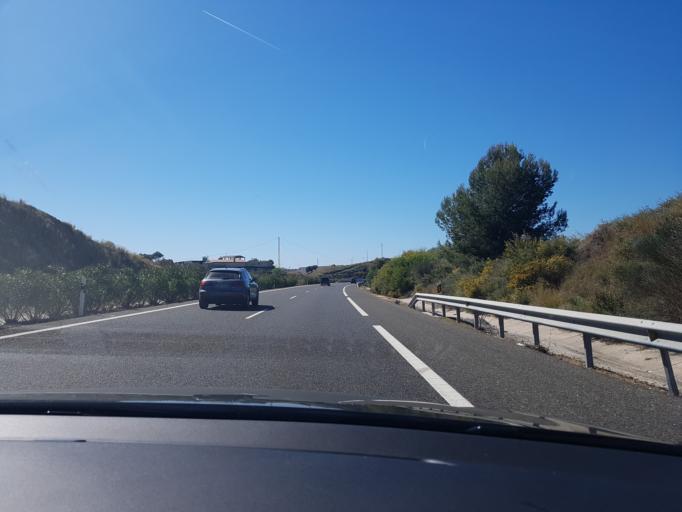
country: ES
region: Andalusia
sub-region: Provincia de Malaga
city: Fuengirola
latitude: 36.5257
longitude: -4.6844
